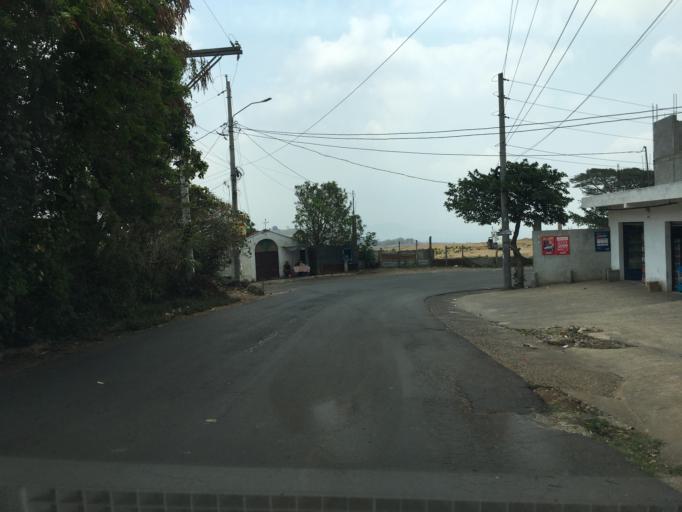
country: GT
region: Escuintla
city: San Vicente Pacaya
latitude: 14.3362
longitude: -90.5661
